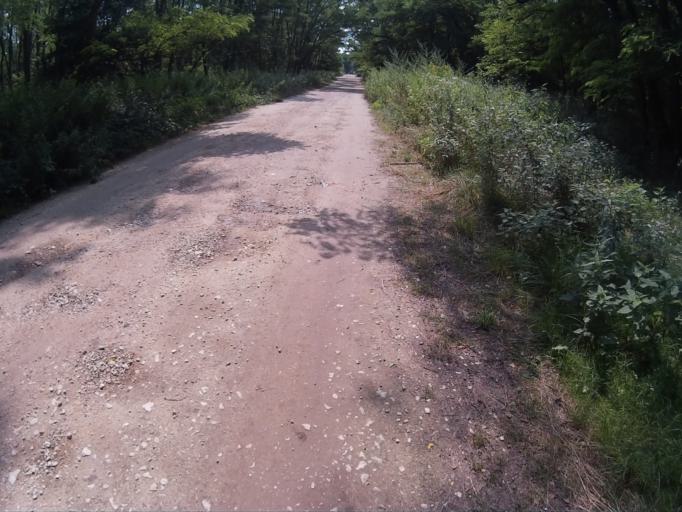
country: HU
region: Veszprem
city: Papa
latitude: 47.2908
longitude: 17.6010
